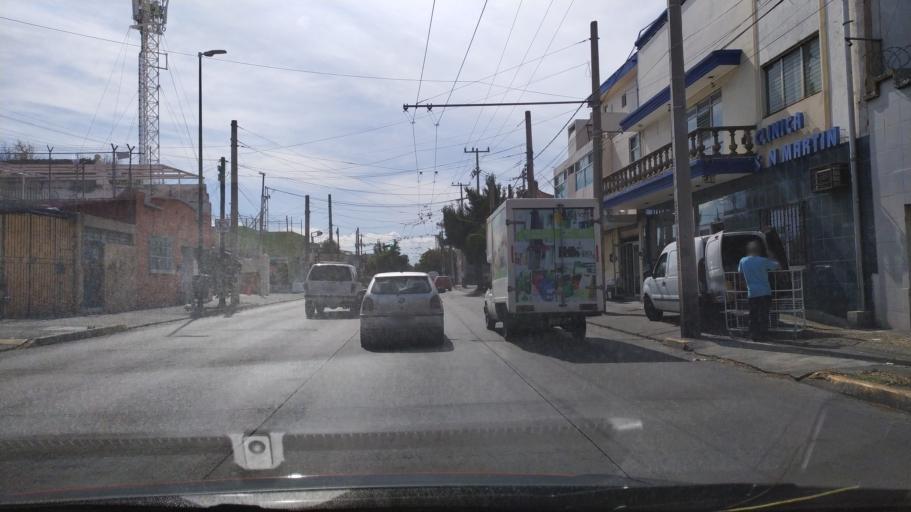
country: MX
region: Jalisco
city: Tlaquepaque
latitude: 20.6786
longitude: -103.3285
